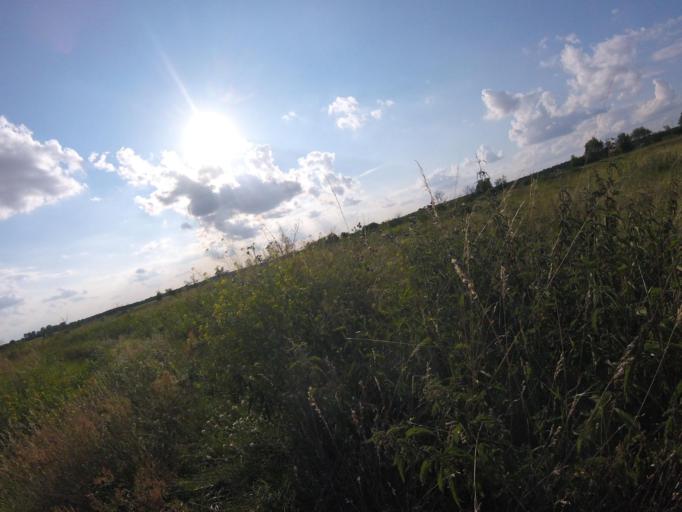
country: DE
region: Brandenburg
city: Mittenwalde
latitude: 52.3121
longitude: 13.5517
